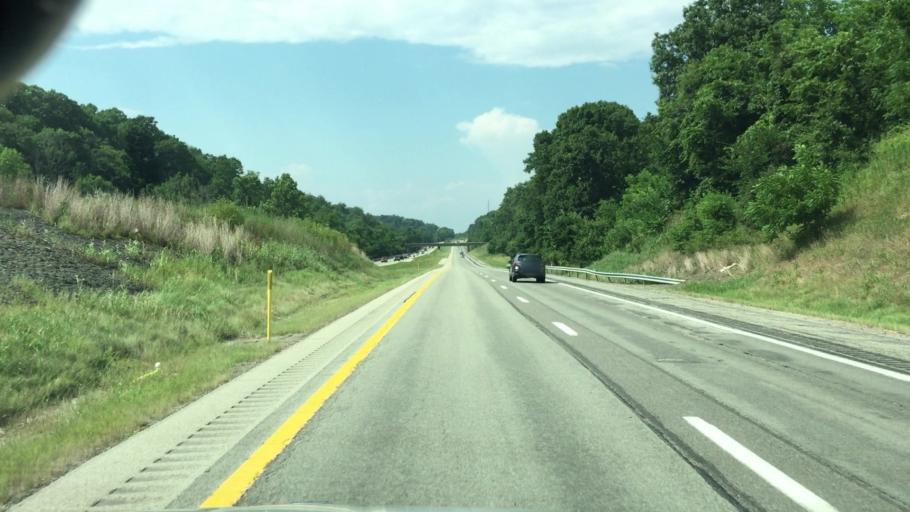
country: US
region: Pennsylvania
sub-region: Washington County
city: East Washington
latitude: 40.0482
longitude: -80.1832
